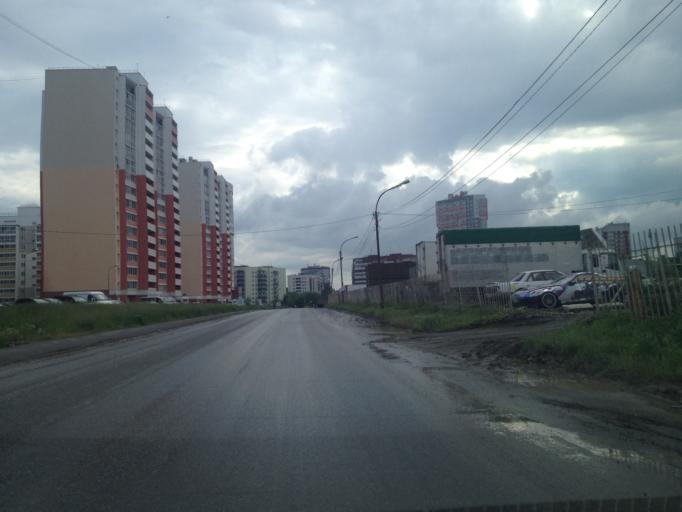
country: RU
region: Sverdlovsk
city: Yekaterinburg
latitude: 56.9102
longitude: 60.6246
